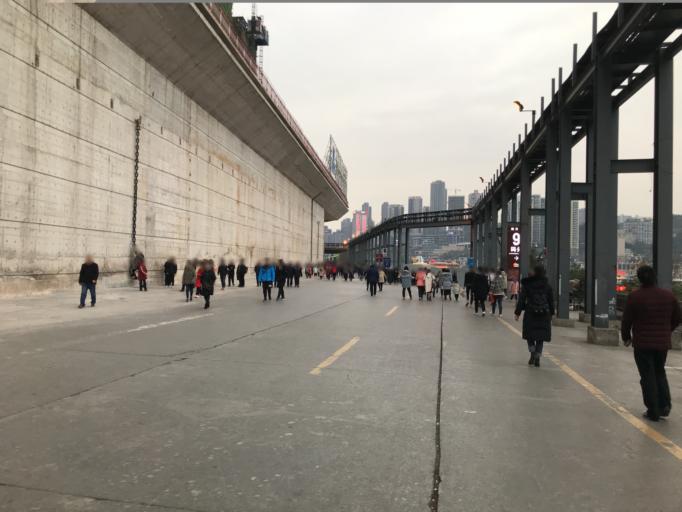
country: CN
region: Chongqing Shi
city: Nanping
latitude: 29.5671
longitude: 106.5854
